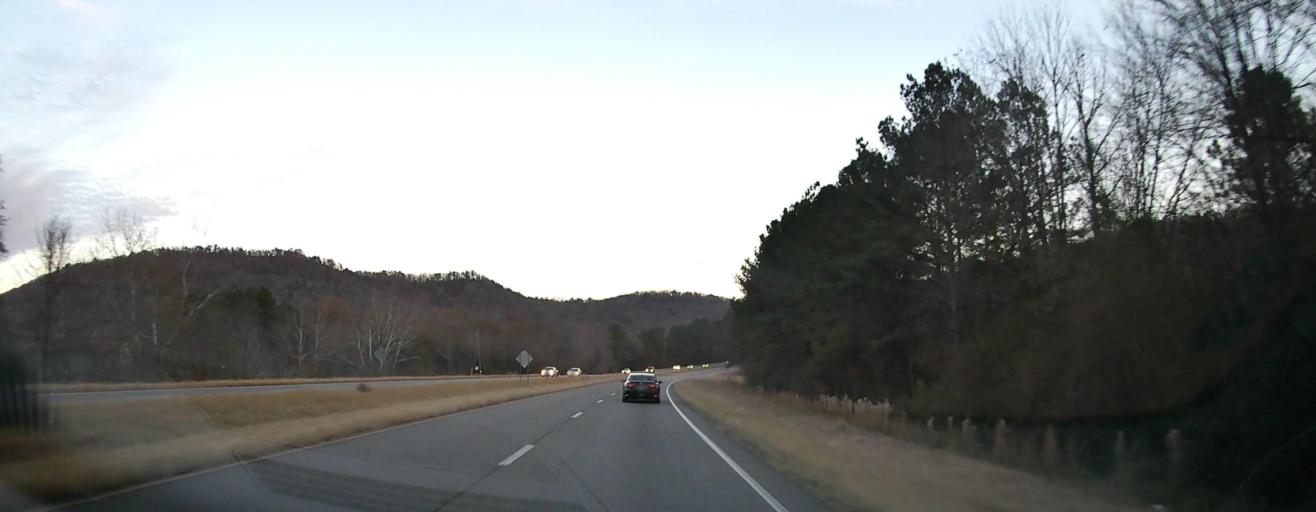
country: US
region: Alabama
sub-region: Etowah County
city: Glencoe
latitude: 33.9428
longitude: -85.9189
